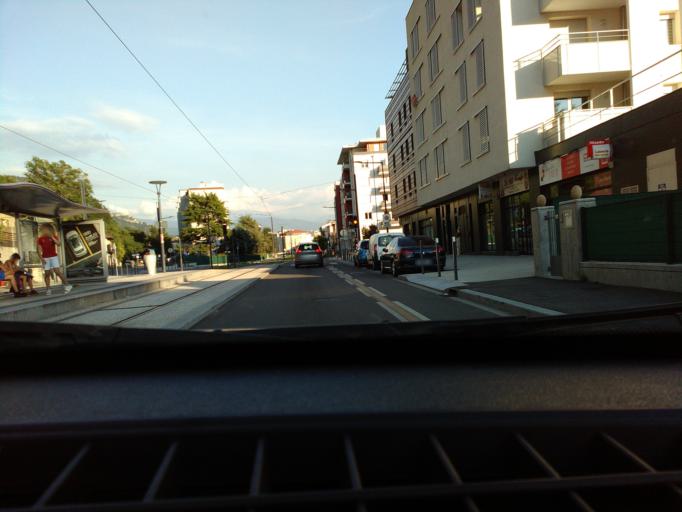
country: FR
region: Rhone-Alpes
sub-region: Departement de l'Isere
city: Saint-Egreve
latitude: 45.2177
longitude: 5.6935
